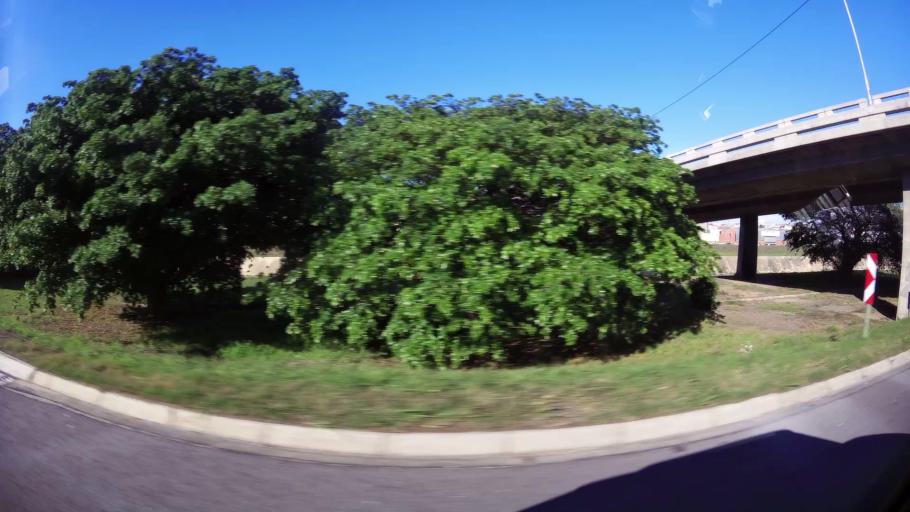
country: ZA
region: Eastern Cape
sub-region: Nelson Mandela Bay Metropolitan Municipality
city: Port Elizabeth
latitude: -33.9138
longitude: 25.6028
